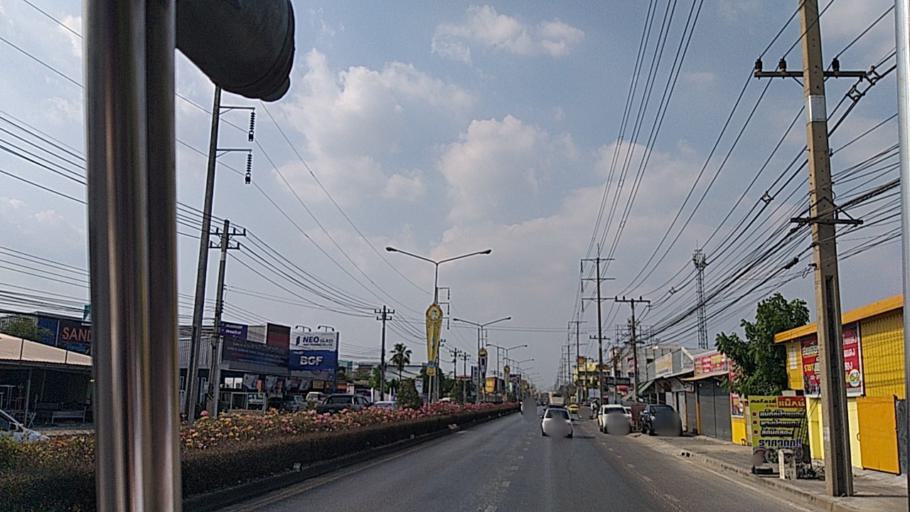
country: TH
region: Pathum Thani
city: Pathum Thani
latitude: 14.0373
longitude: 100.5253
